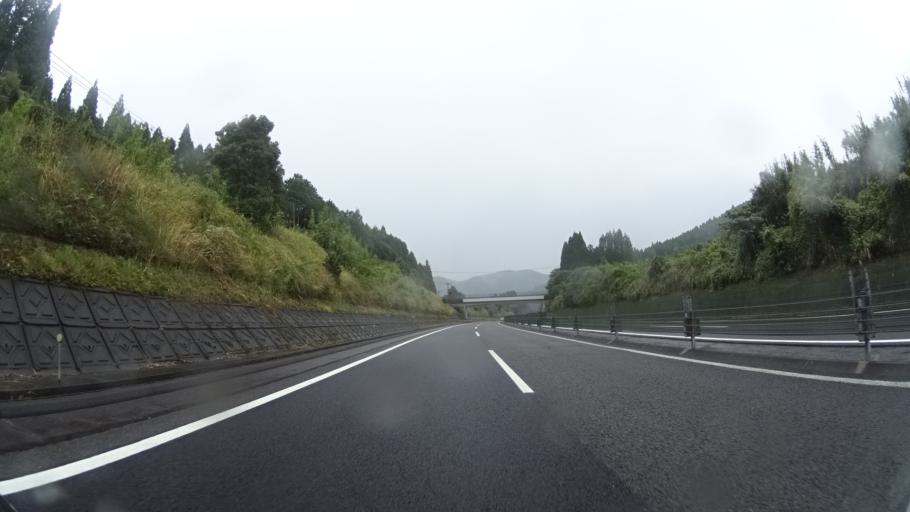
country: JP
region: Kagoshima
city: Okuchi-shinohara
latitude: 31.9557
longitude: 130.7362
